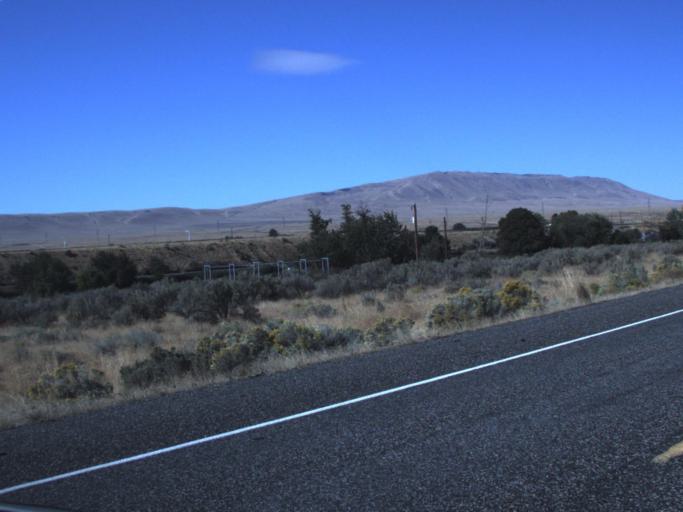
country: US
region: Washington
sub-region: Benton County
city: West Richland
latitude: 46.3766
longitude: -119.4105
